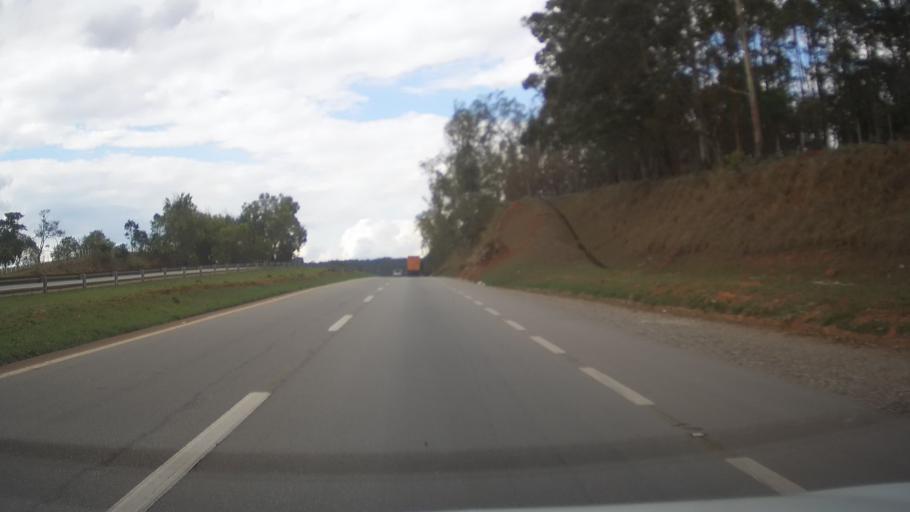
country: BR
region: Minas Gerais
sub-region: Itauna
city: Itauna
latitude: -20.2932
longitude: -44.4367
